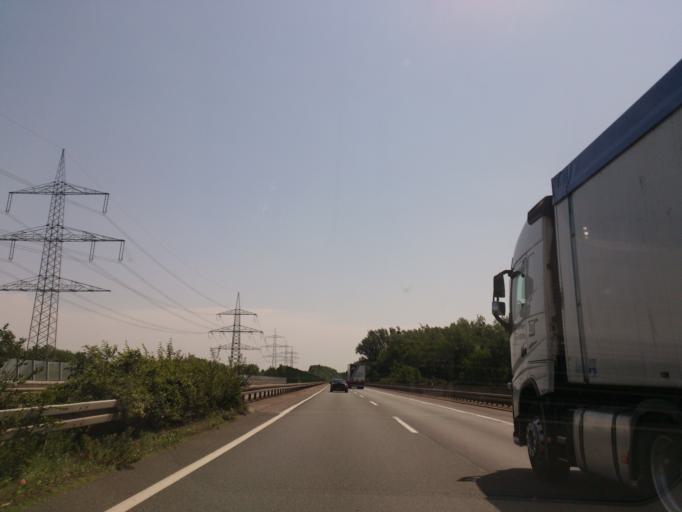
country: DE
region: North Rhine-Westphalia
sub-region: Regierungsbezirk Detmold
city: Paderborn
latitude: 51.6972
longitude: 8.7075
